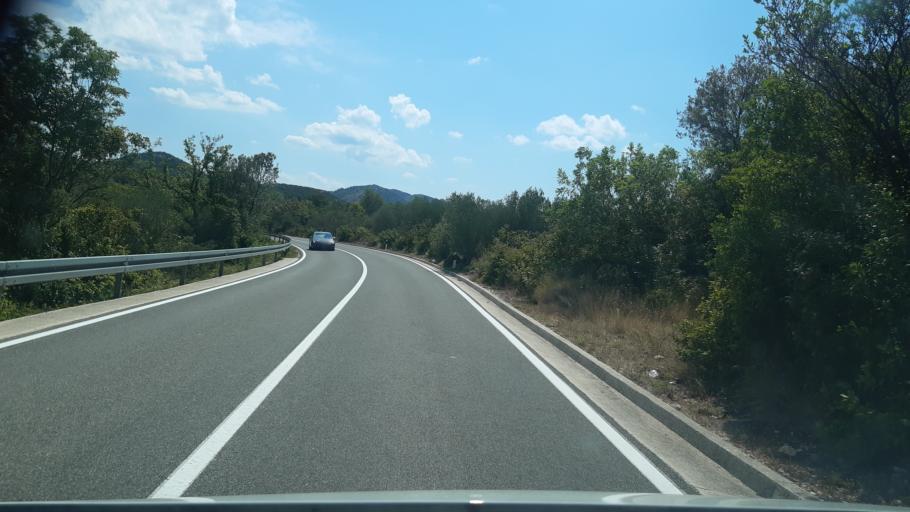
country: HR
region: Dubrovacko-Neretvanska
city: Ston
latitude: 42.8346
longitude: 17.7225
